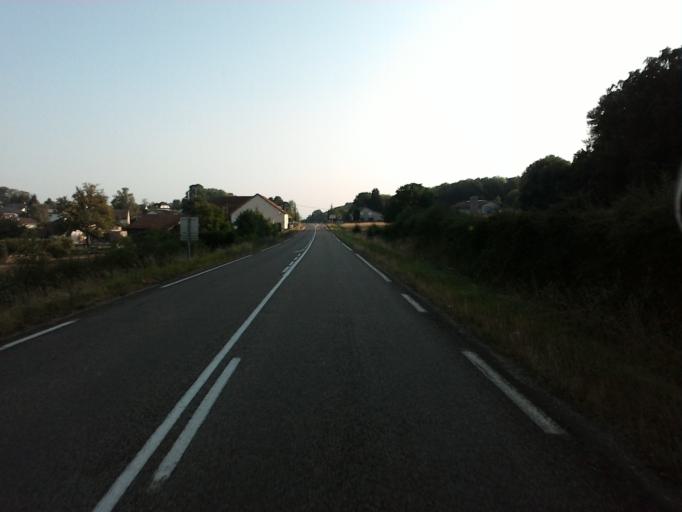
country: FR
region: Franche-Comte
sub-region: Departement de la Haute-Saone
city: Echenoz-la-Meline
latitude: 47.5871
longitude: 6.1381
